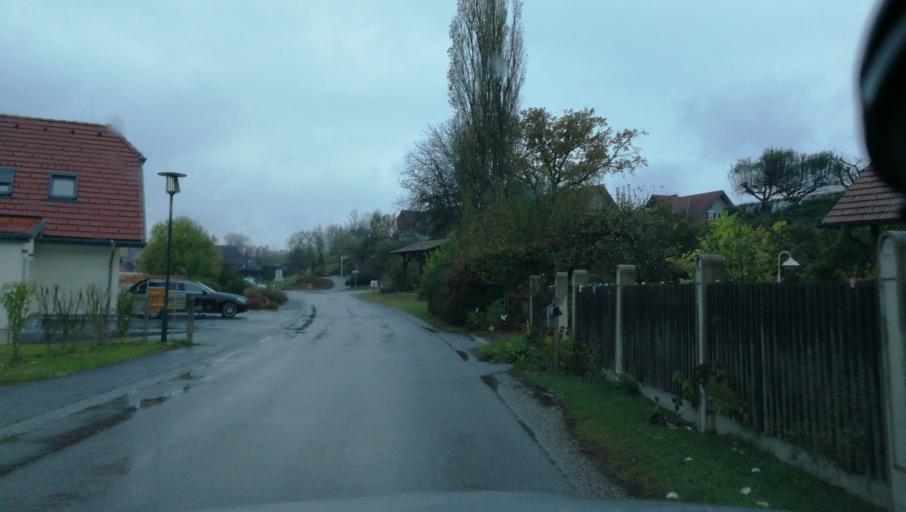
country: AT
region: Styria
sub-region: Politischer Bezirk Leibnitz
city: Sankt Veit am Vogau
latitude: 46.7474
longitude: 15.6291
